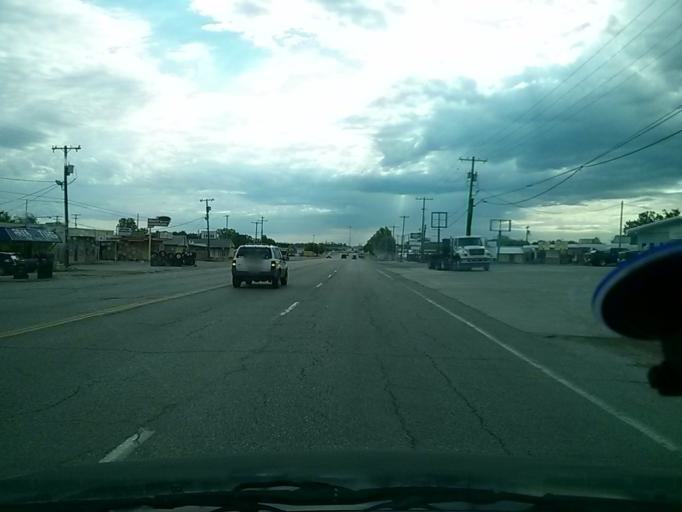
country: US
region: Oklahoma
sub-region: Tulsa County
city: Owasso
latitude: 36.1607
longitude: -95.8774
